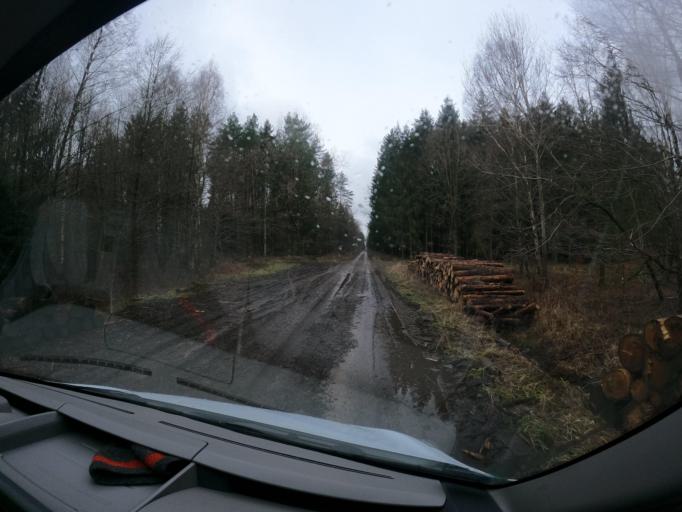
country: PL
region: West Pomeranian Voivodeship
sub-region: Powiat slawienski
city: Slawno
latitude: 54.4120
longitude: 16.5912
